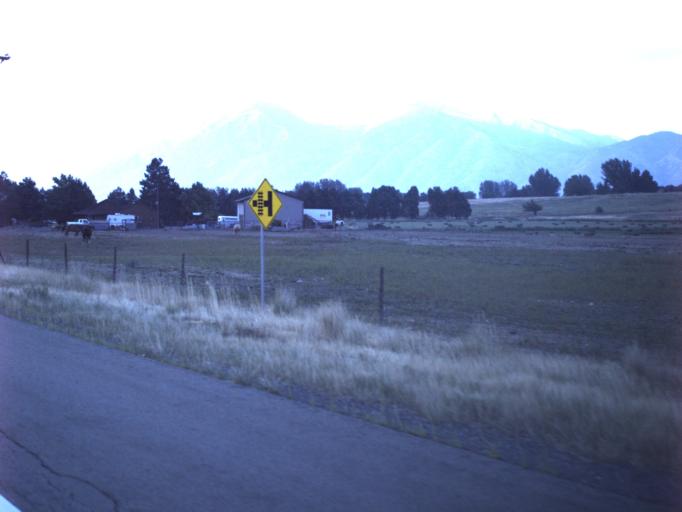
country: US
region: Utah
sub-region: Utah County
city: Mapleton
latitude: 40.1013
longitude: -111.5964
